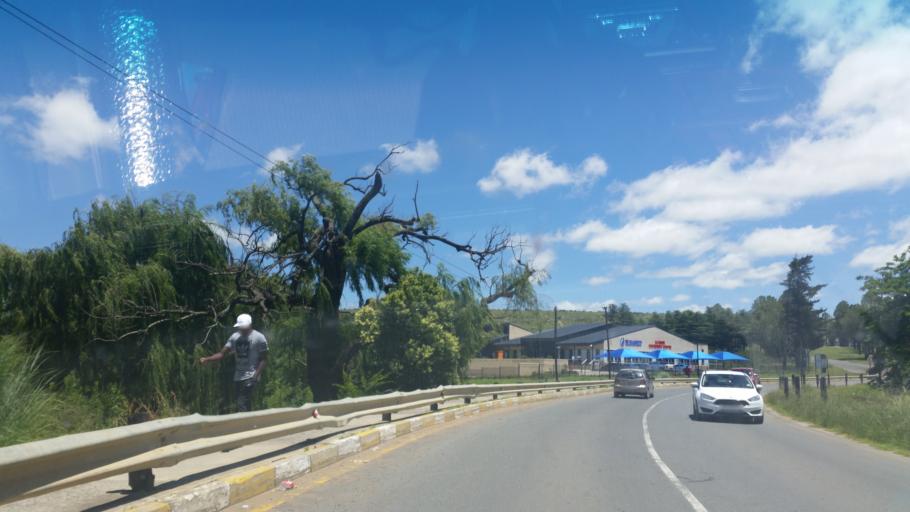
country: ZA
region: Orange Free State
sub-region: Thabo Mofutsanyana District Municipality
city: Harrismith
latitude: -28.2626
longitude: 29.1177
